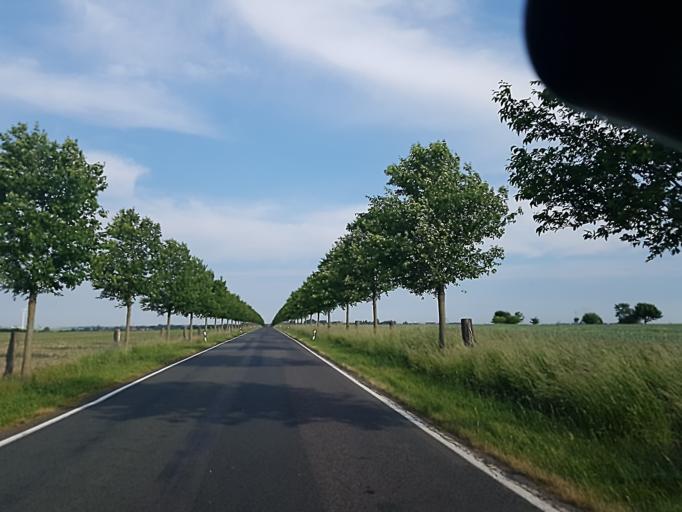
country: DE
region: Saxony-Anhalt
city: Kropstadt
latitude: 51.9902
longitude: 12.7939
